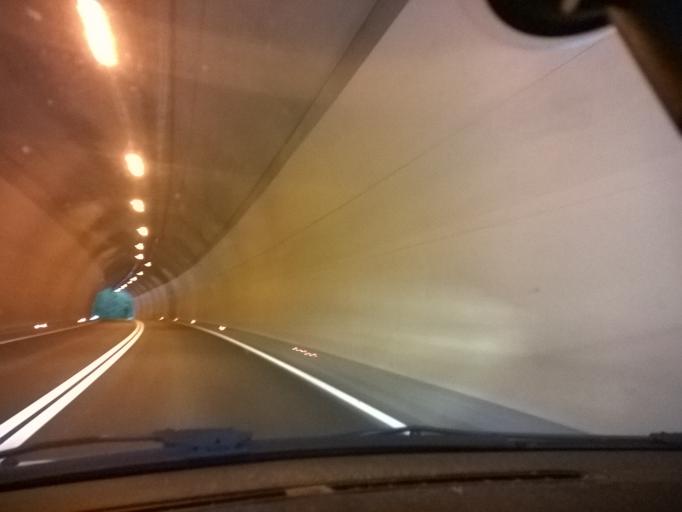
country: SI
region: Zetale
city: Zetale
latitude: 46.2474
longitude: 15.8501
